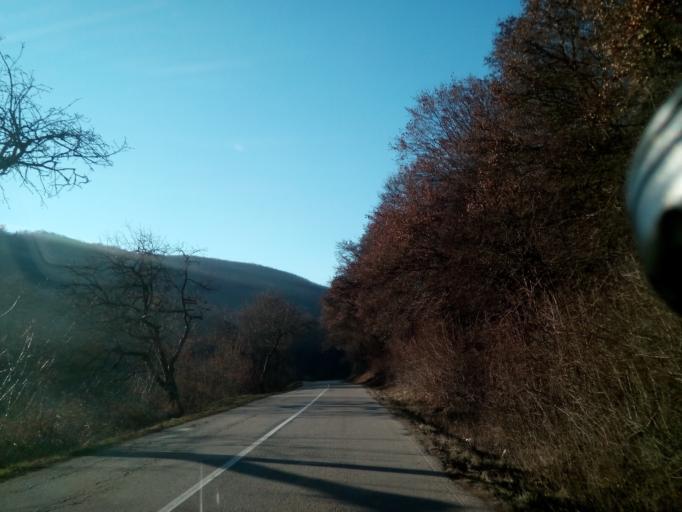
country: SK
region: Kosicky
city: Medzev
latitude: 48.6918
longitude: 20.9582
